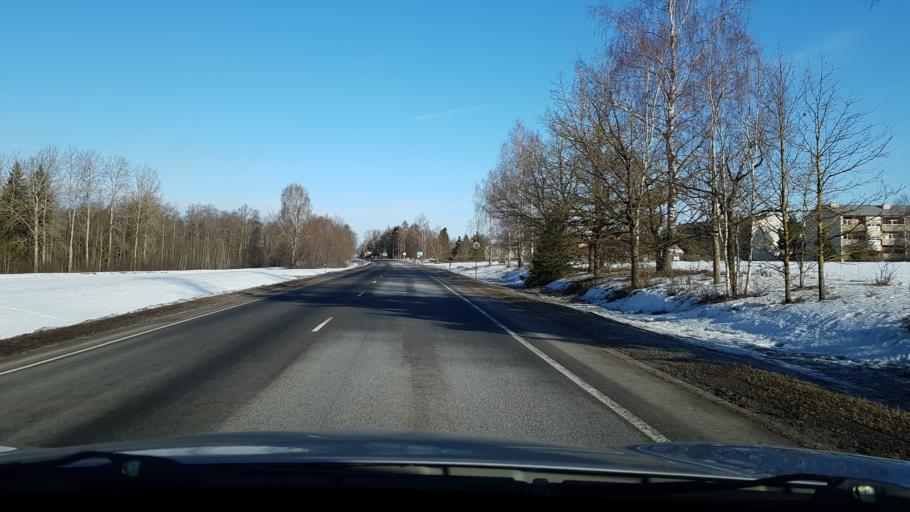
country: EE
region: Jogevamaa
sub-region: Poltsamaa linn
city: Poltsamaa
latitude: 58.7290
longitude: 25.7657
